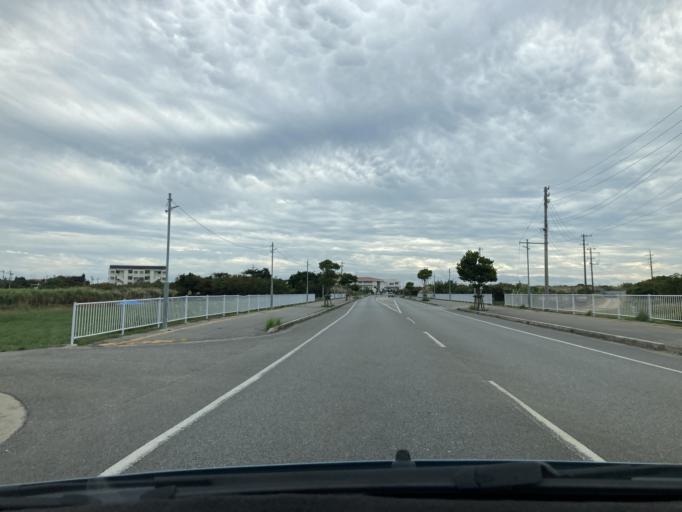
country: JP
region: Okinawa
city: Ishikawa
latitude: 26.4004
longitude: 127.7395
